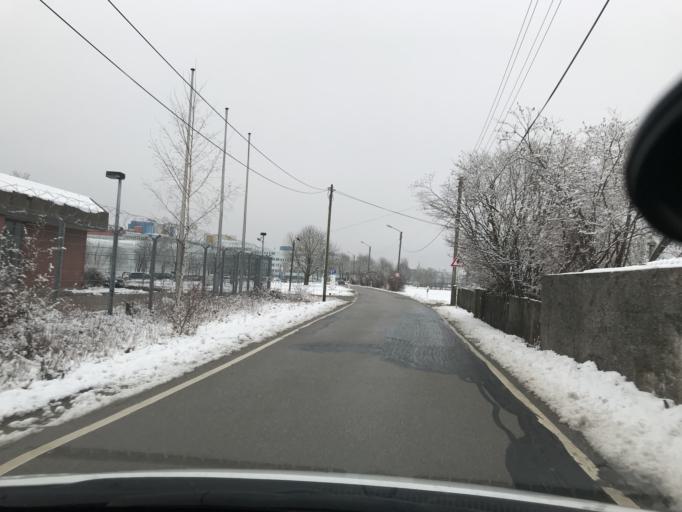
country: DE
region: Bavaria
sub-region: Upper Bavaria
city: Neubiberg
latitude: 48.0854
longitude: 11.6495
